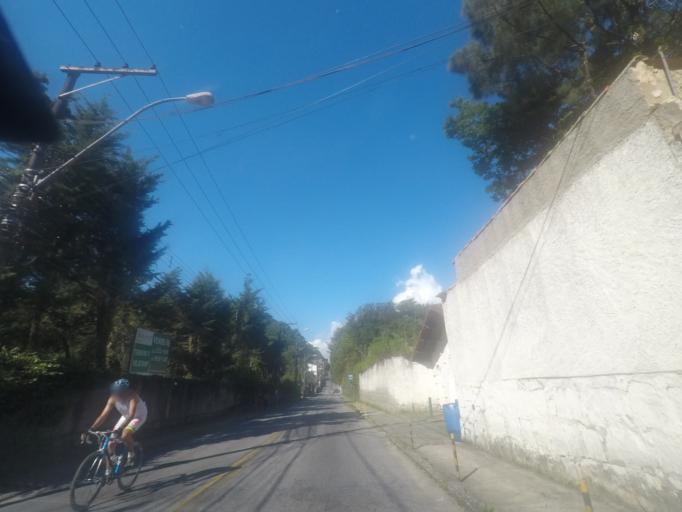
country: BR
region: Rio de Janeiro
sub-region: Petropolis
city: Petropolis
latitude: -22.5332
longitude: -43.1948
